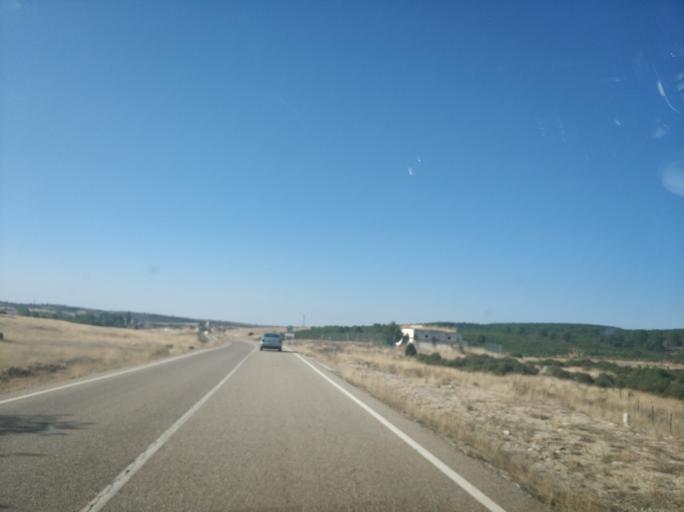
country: ES
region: Castille and Leon
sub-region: Provincia de Soria
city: Santa Maria de las Hoyas
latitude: 41.7784
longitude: -3.1350
